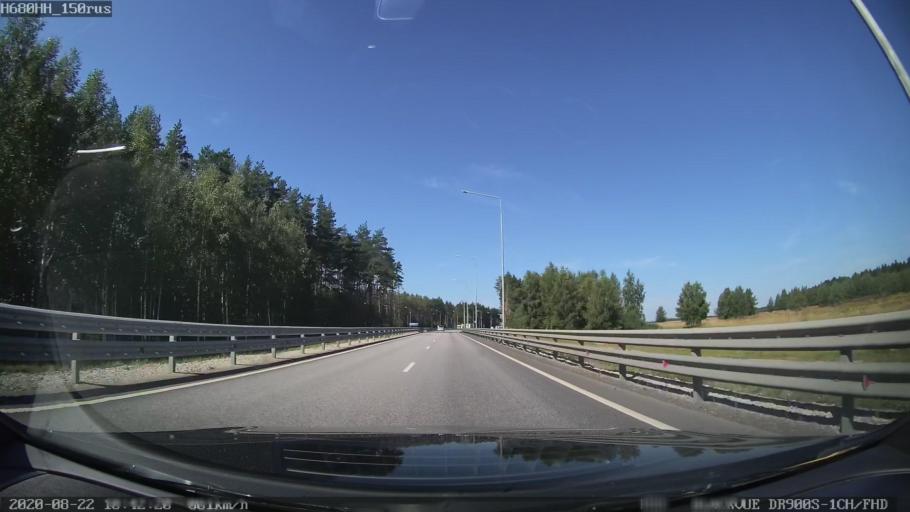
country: RU
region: Tverskaya
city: Gorodnya
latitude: 56.7362
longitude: 36.2620
